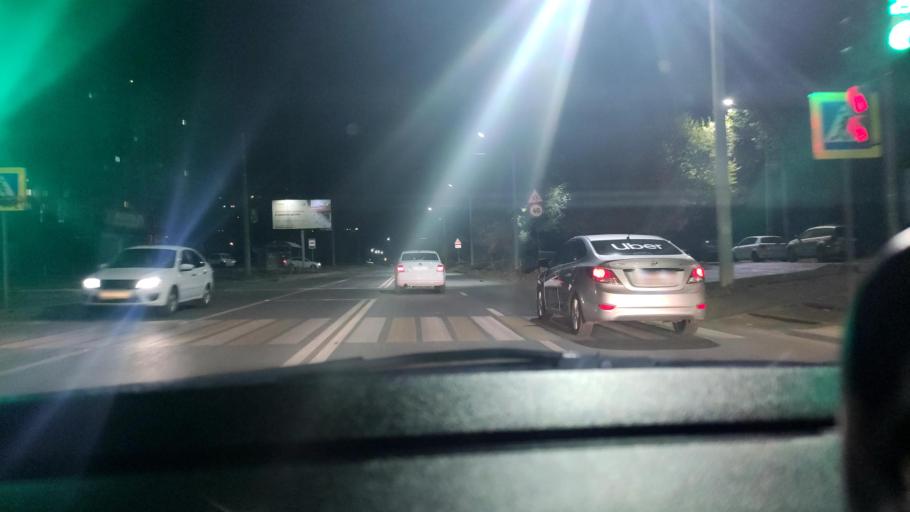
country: RU
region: Voronezj
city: Podgornoye
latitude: 51.7136
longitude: 39.1620
